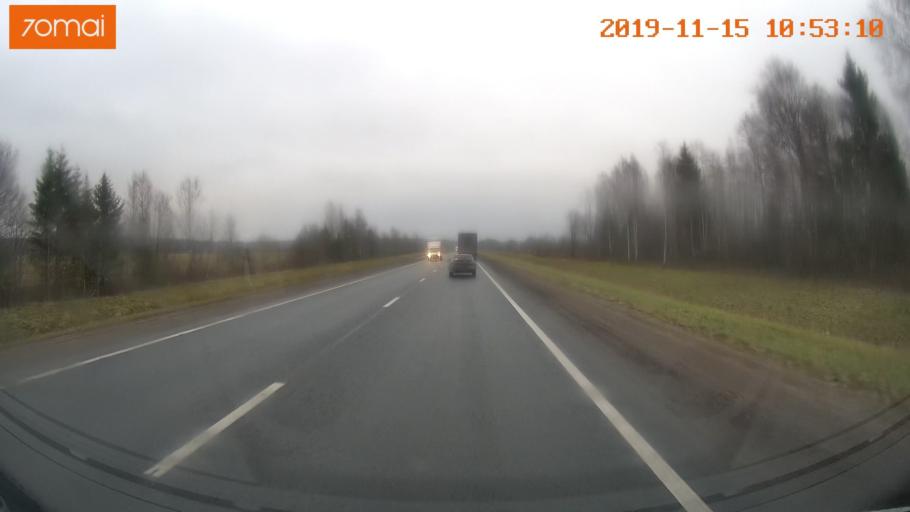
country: RU
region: Vologda
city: Chebsara
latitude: 59.1705
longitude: 38.7487
